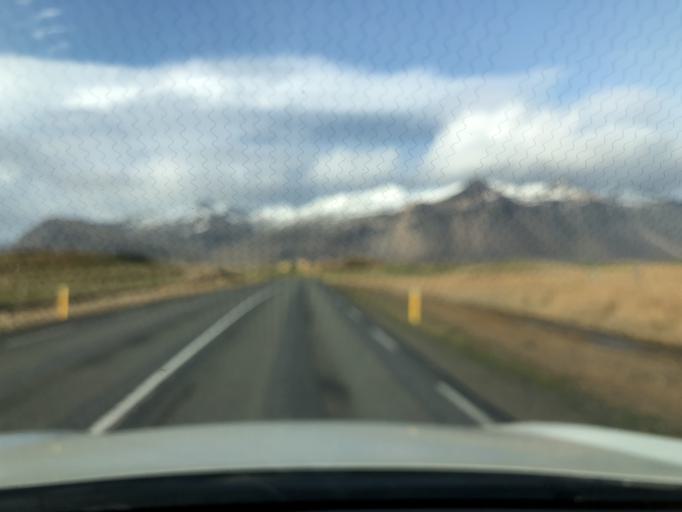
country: IS
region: East
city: Hoefn
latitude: 64.2815
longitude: -15.1915
